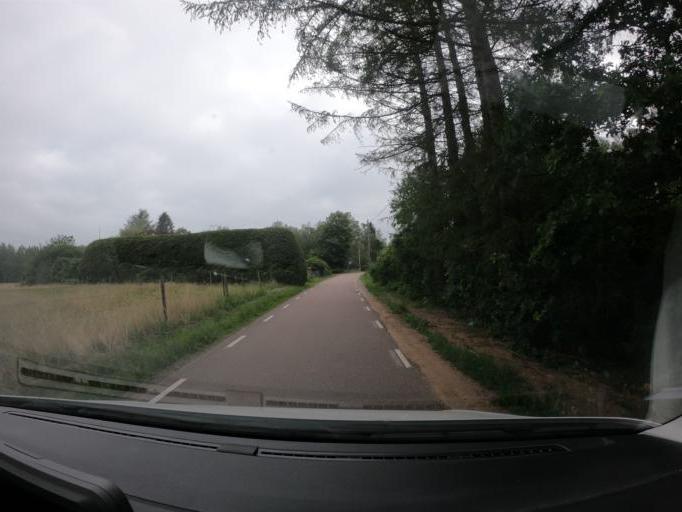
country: SE
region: Skane
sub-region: Perstorps Kommun
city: Perstorp
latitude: 56.0479
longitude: 13.3576
